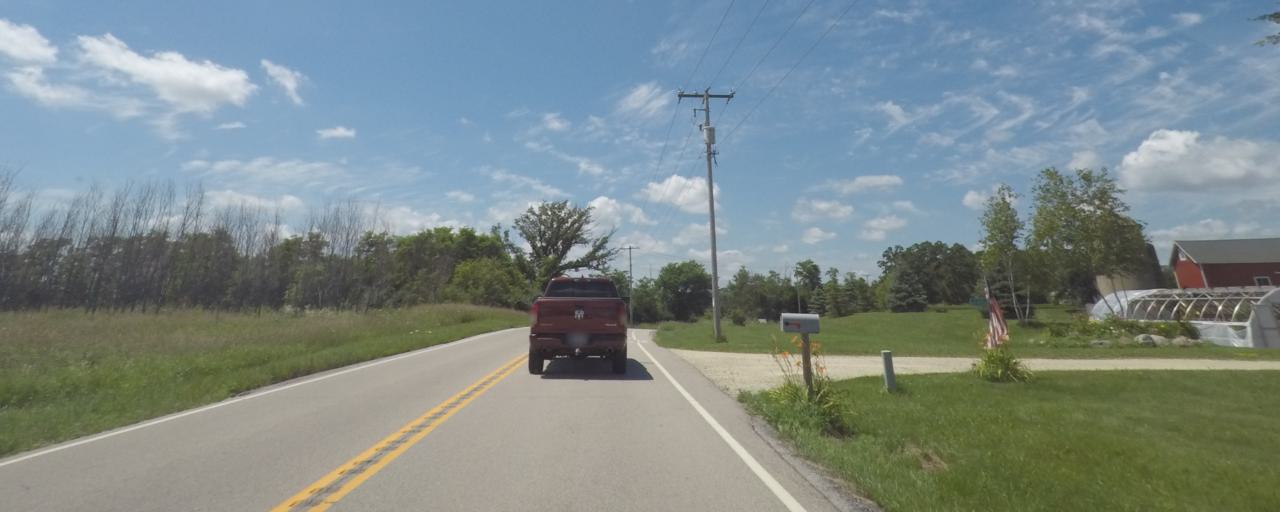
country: US
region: Wisconsin
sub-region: Waukesha County
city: Eagle
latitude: 42.9264
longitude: -88.5293
